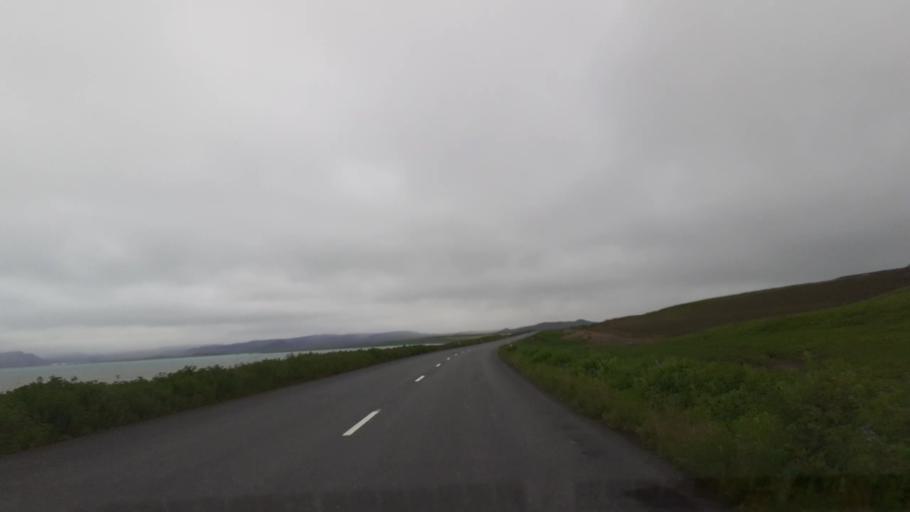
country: IS
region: Northeast
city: Husavik
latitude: 66.2199
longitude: -16.4591
